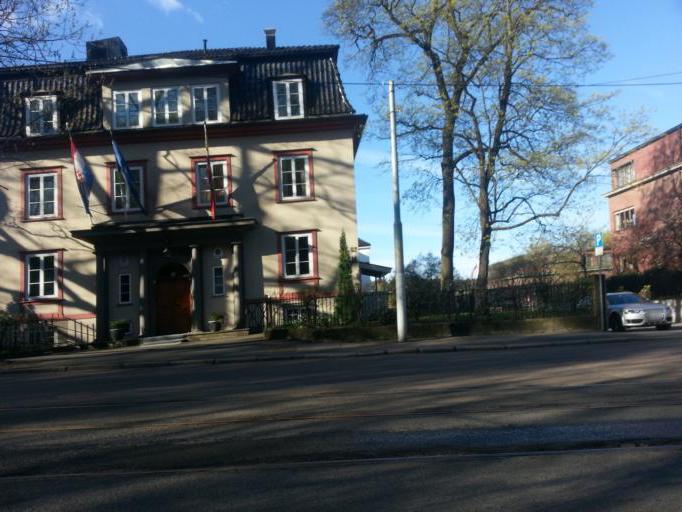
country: NO
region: Oslo
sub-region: Oslo
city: Sjolyststranda
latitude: 59.9142
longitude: 10.7030
